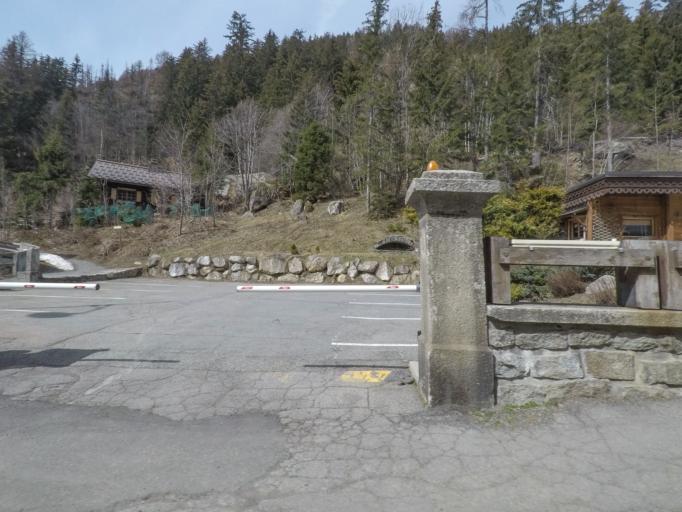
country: FR
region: Rhone-Alpes
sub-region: Departement de la Haute-Savoie
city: Chamonix-Mont-Blanc
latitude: 45.9839
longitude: 6.9266
